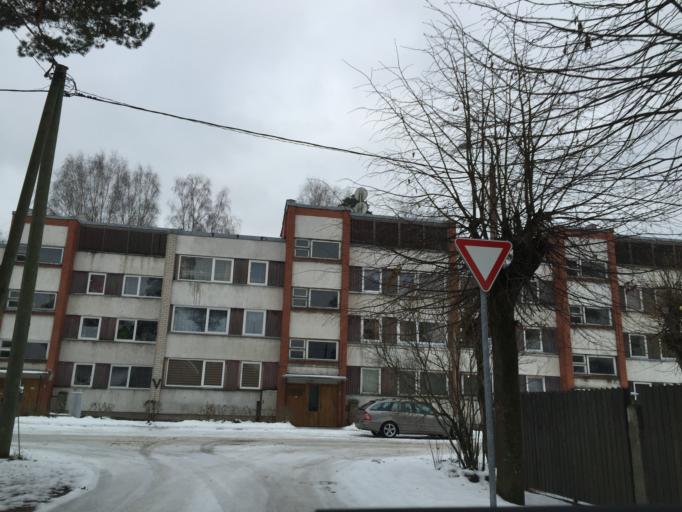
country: LV
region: Saulkrastu
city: Saulkrasti
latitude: 57.2656
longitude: 24.4160
